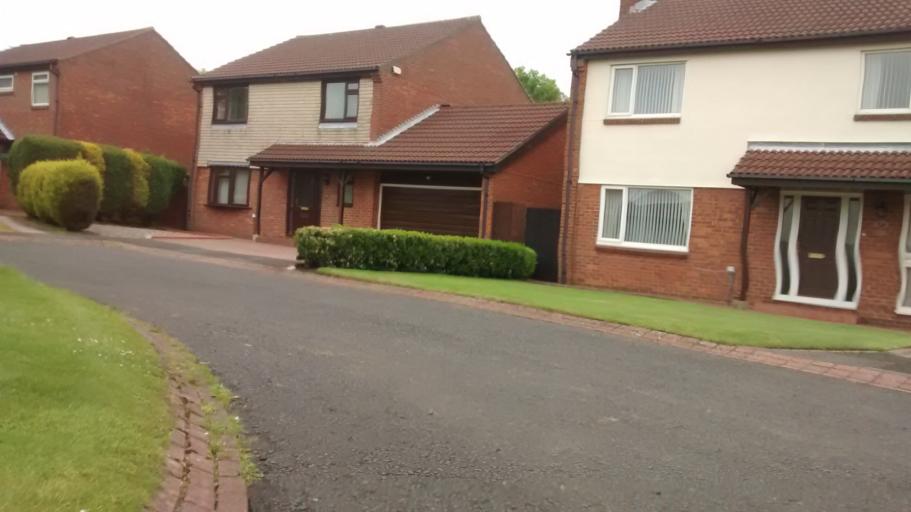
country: GB
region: England
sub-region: County Durham
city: Pittington
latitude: 54.7904
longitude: -1.4921
